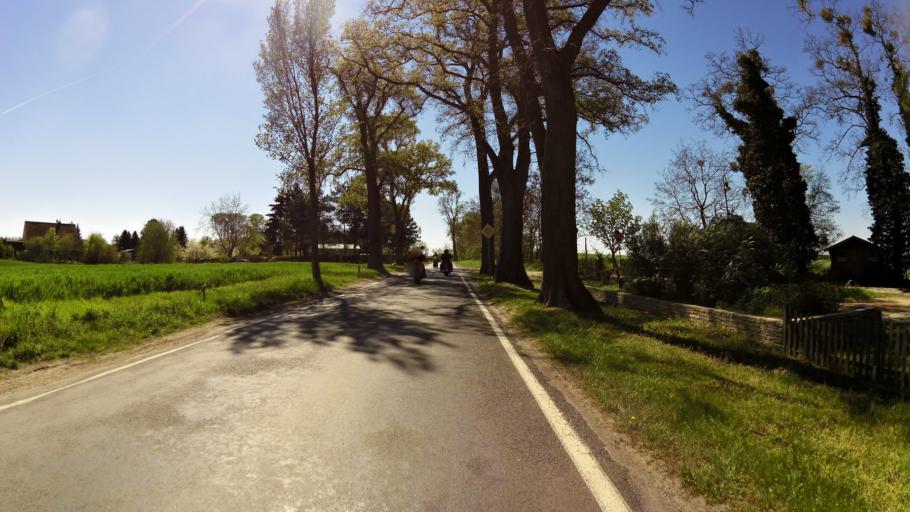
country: DE
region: Brandenburg
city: Werftpfuhl
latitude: 52.6424
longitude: 13.7927
